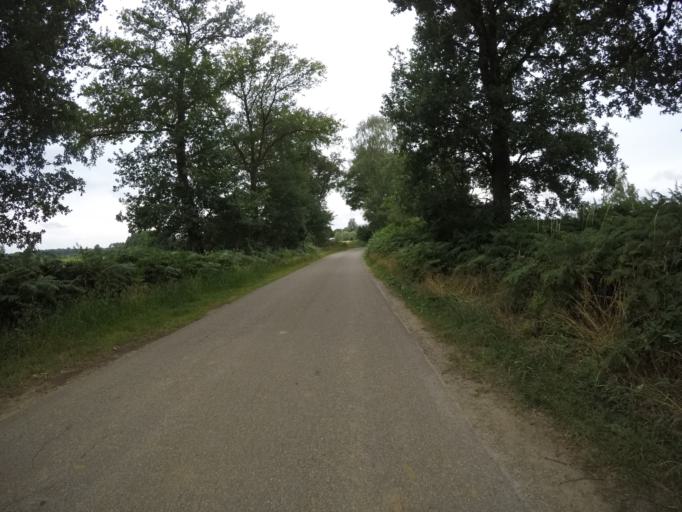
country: DE
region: North Rhine-Westphalia
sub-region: Regierungsbezirk Munster
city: Isselburg
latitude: 51.8521
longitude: 6.4456
